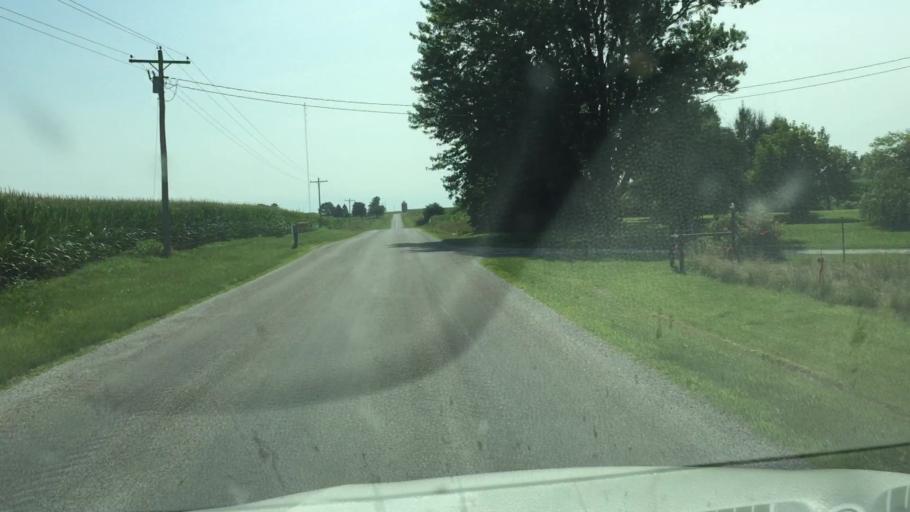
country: US
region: Illinois
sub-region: Hancock County
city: Nauvoo
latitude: 40.5113
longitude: -91.3369
